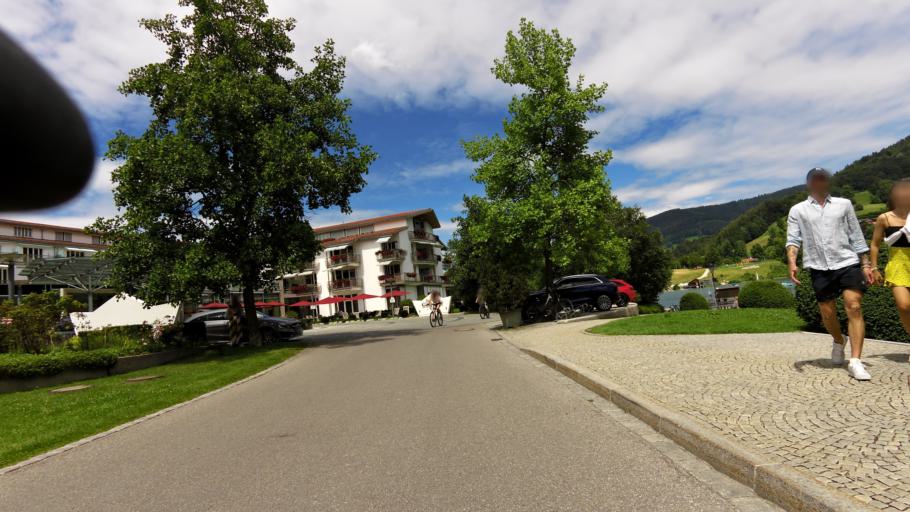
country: DE
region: Bavaria
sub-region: Upper Bavaria
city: Rottach-Egern
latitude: 47.6966
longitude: 11.7587
